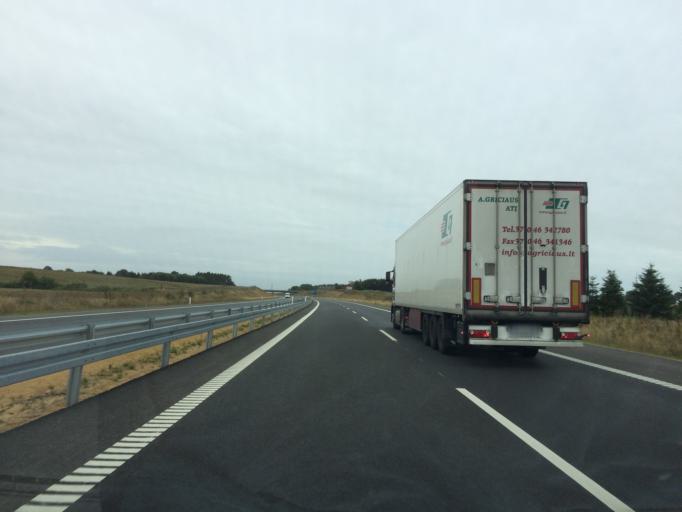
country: DK
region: Central Jutland
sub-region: Herning Kommune
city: Snejbjerg
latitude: 56.1406
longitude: 8.8692
